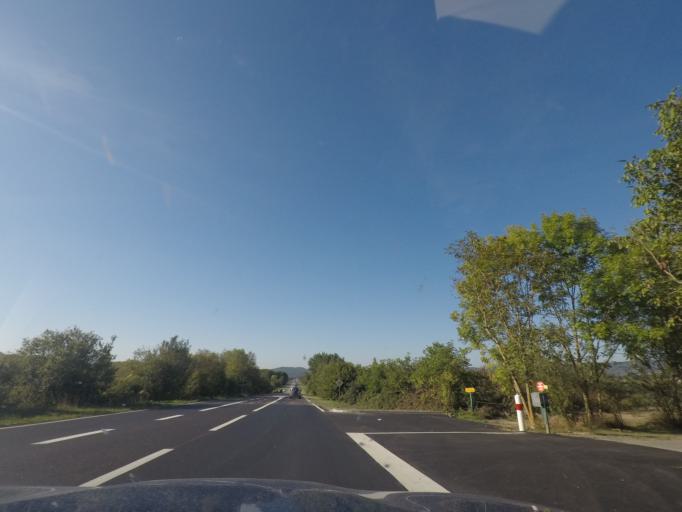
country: FR
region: Lorraine
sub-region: Departement de la Moselle
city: Hettange-Grande
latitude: 49.4248
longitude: 6.1634
